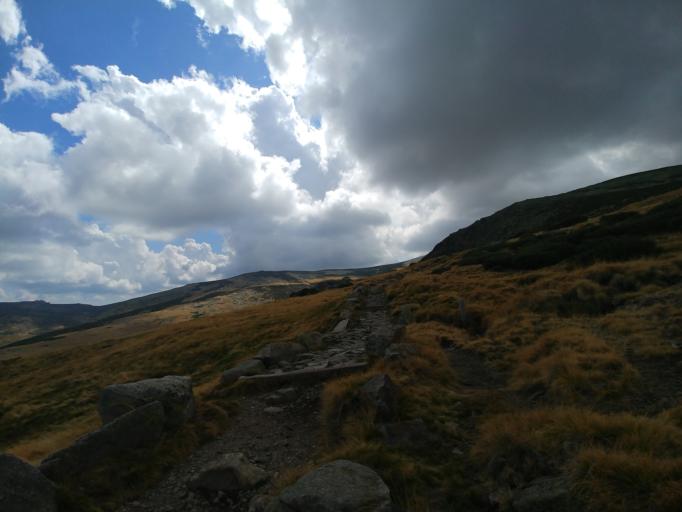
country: ES
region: Castille and Leon
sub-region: Provincia de Avila
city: Navalperal de Tormes
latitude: 40.2719
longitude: -5.2505
